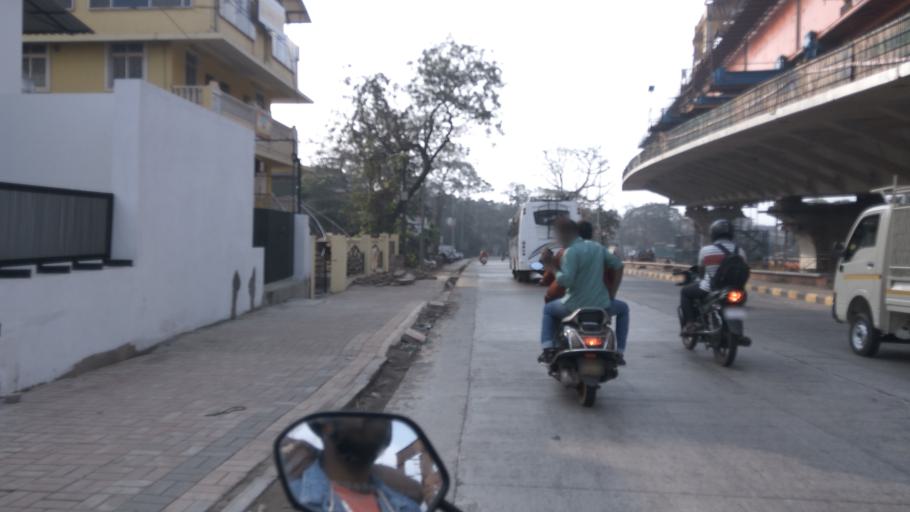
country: IN
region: Goa
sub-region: North Goa
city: Panaji
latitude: 15.5152
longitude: 73.8352
